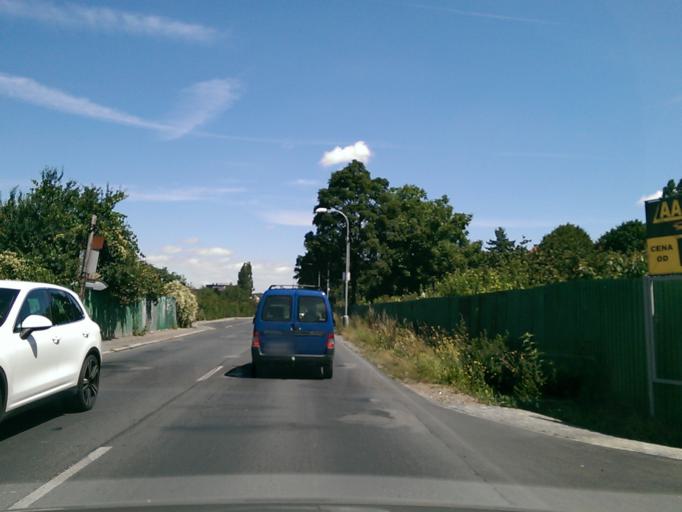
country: CZ
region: Praha
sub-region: Praha 8
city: Liben
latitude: 50.0982
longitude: 14.4816
